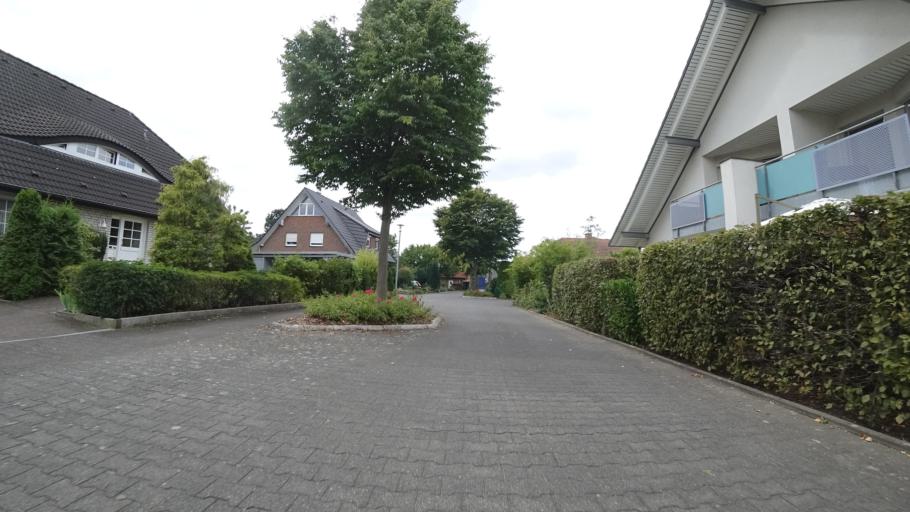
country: DE
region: North Rhine-Westphalia
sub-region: Regierungsbezirk Detmold
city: Verl
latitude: 51.9382
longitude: 8.4648
